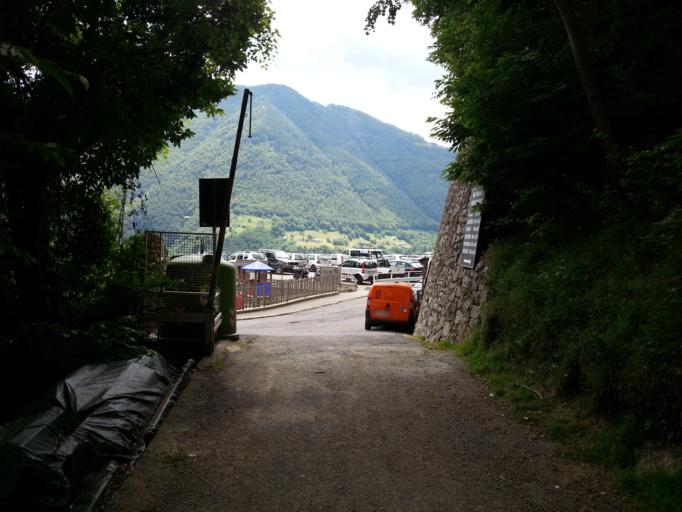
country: IT
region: Lombardy
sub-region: Provincia di Lecco
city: Premana
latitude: 46.0520
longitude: 9.4325
